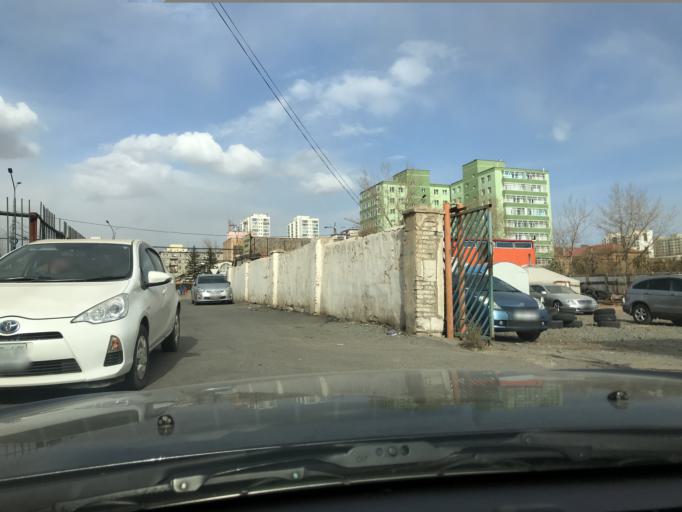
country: MN
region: Ulaanbaatar
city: Ulaanbaatar
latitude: 47.9168
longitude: 106.9524
